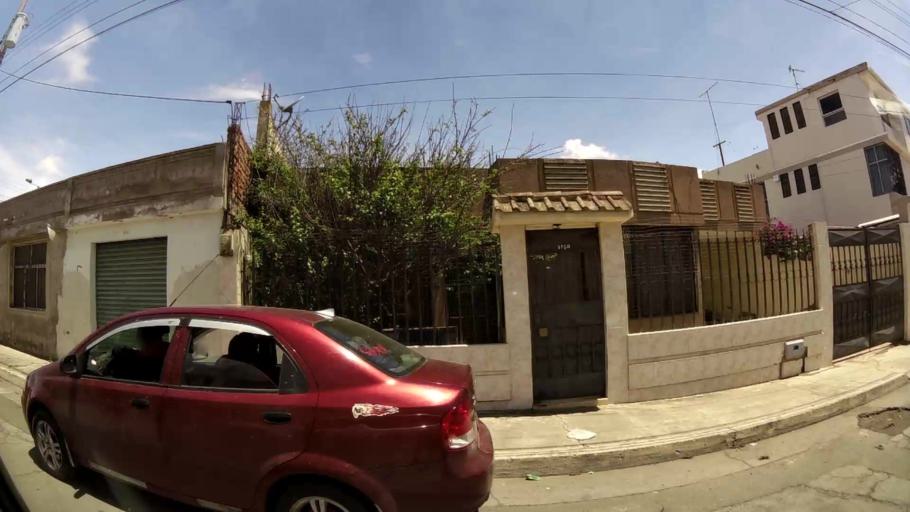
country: EC
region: Chimborazo
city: Riobamba
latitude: -1.6749
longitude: -78.6596
